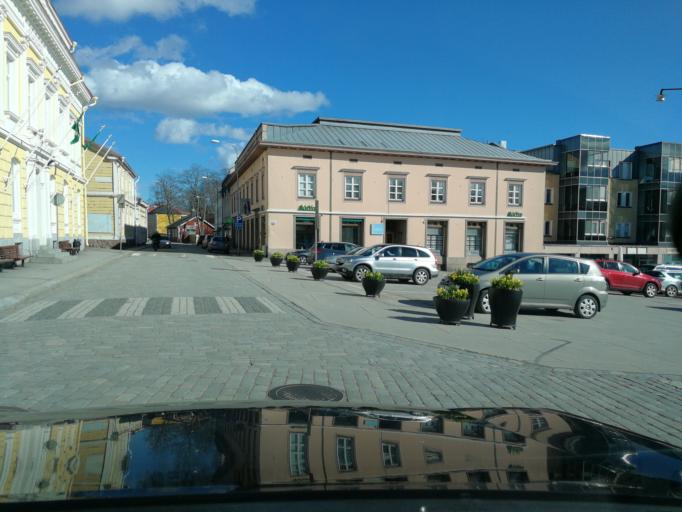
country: FI
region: Uusimaa
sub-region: Raaseporin
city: Ekenaes
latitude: 59.9746
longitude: 23.4356
